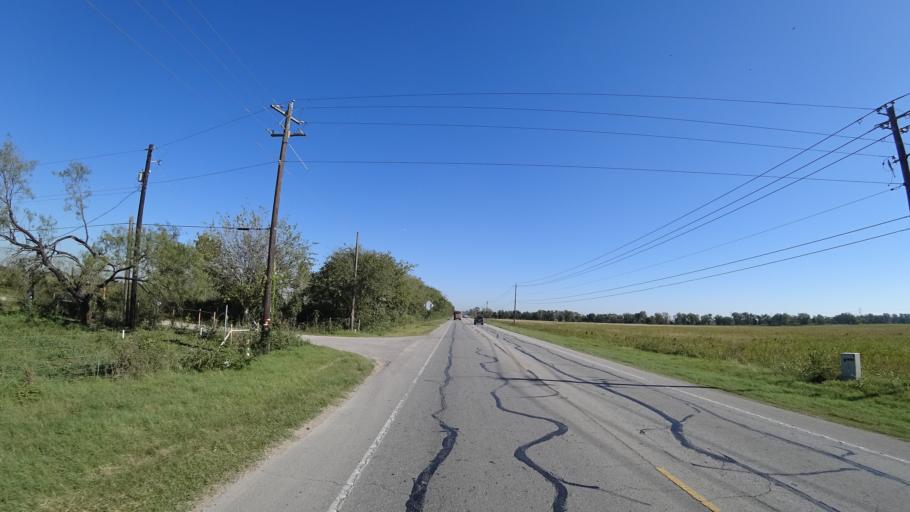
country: US
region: Texas
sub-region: Travis County
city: Hornsby Bend
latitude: 30.2371
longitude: -97.6245
